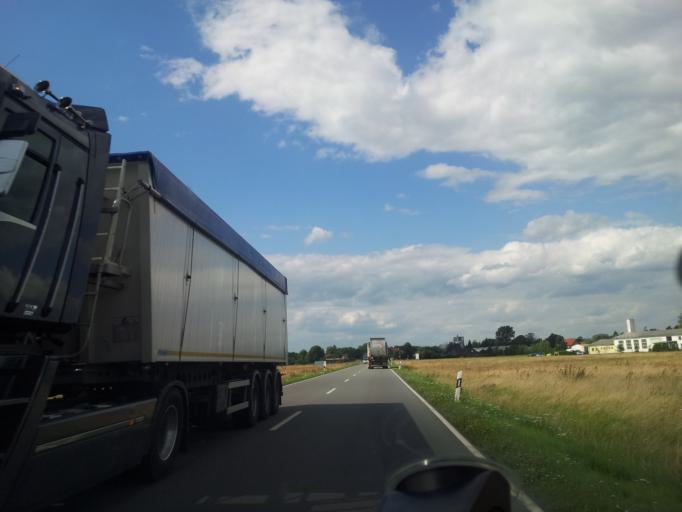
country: DE
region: Saxony-Anhalt
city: Gross Ammensleben
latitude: 52.2687
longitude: 11.4726
